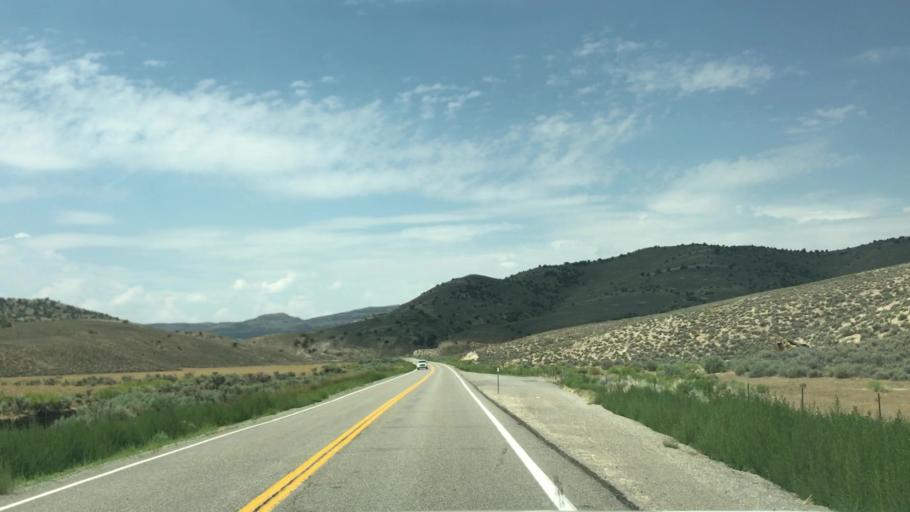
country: US
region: Nevada
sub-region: White Pine County
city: Ely
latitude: 39.3520
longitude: -115.3701
